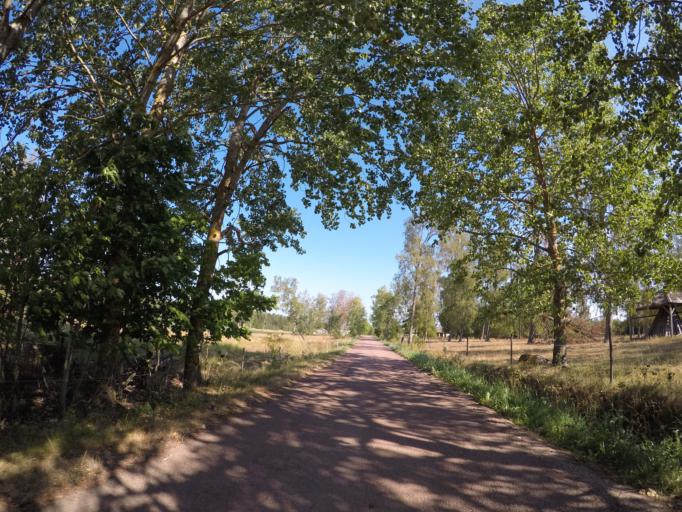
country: AX
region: Alands landsbygd
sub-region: Finstroem
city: Finstroem
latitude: 60.2782
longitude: 19.9572
